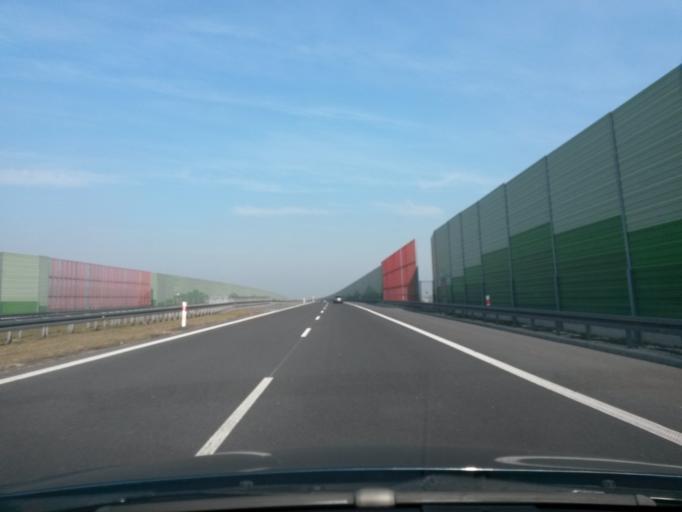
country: PL
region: Lodz Voivodeship
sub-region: Powiat leczycki
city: Piatek
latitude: 52.1094
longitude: 19.5088
